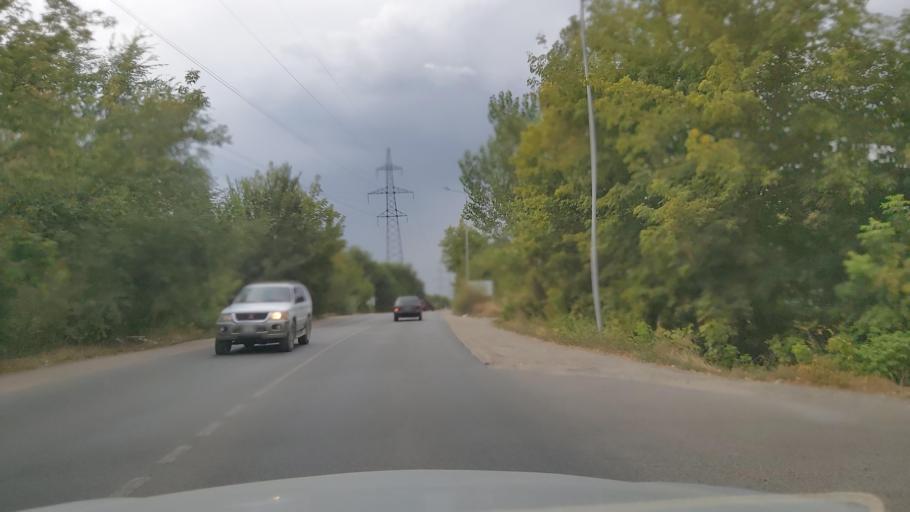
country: KZ
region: Almaty Oblysy
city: Energeticheskiy
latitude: 43.4036
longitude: 77.0262
